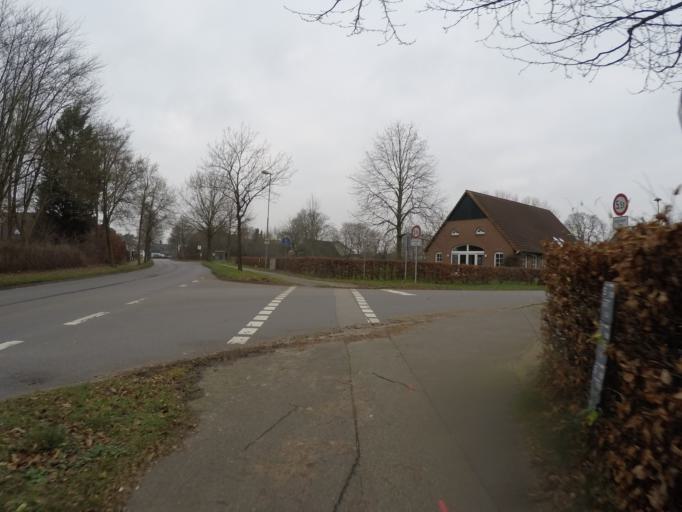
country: DE
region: Schleswig-Holstein
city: Quickborn
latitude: 53.7214
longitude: 9.8655
